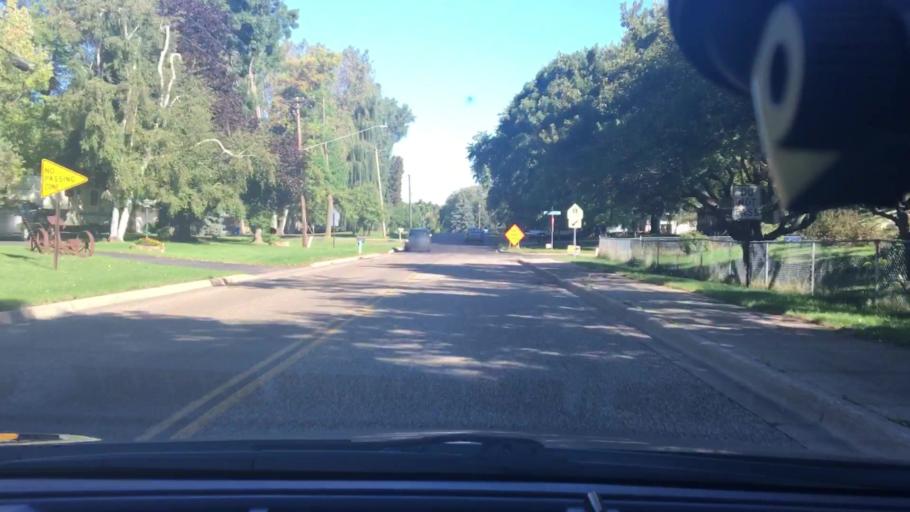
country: US
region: Minnesota
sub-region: Hennepin County
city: Plymouth
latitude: 44.9782
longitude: -93.4476
